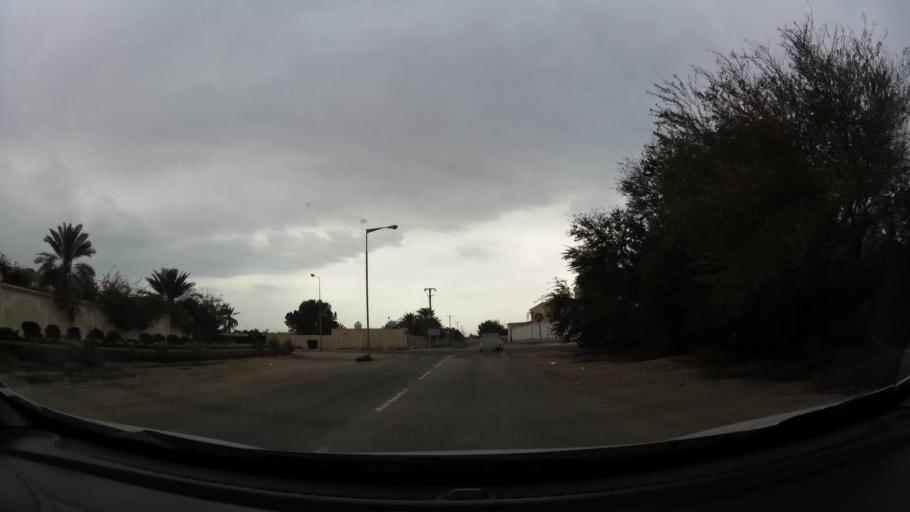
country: BH
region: Central Governorate
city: Madinat Hamad
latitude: 26.1501
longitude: 50.4651
